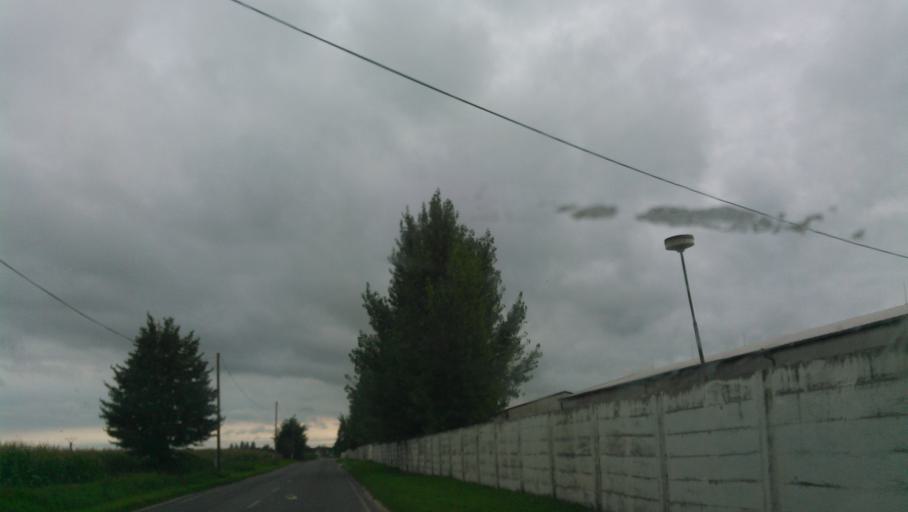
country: SK
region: Trnavsky
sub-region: Okres Dunajska Streda
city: Velky Meder
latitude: 47.9309
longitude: 17.7280
